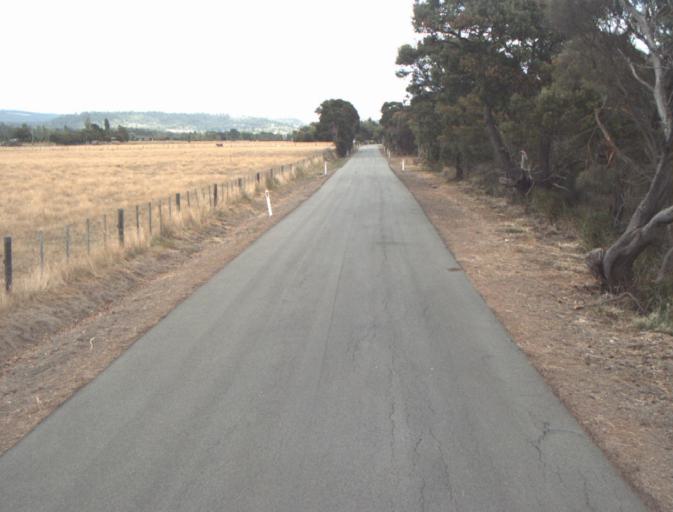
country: AU
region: Tasmania
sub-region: Launceston
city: Mayfield
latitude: -41.2833
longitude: 147.0072
